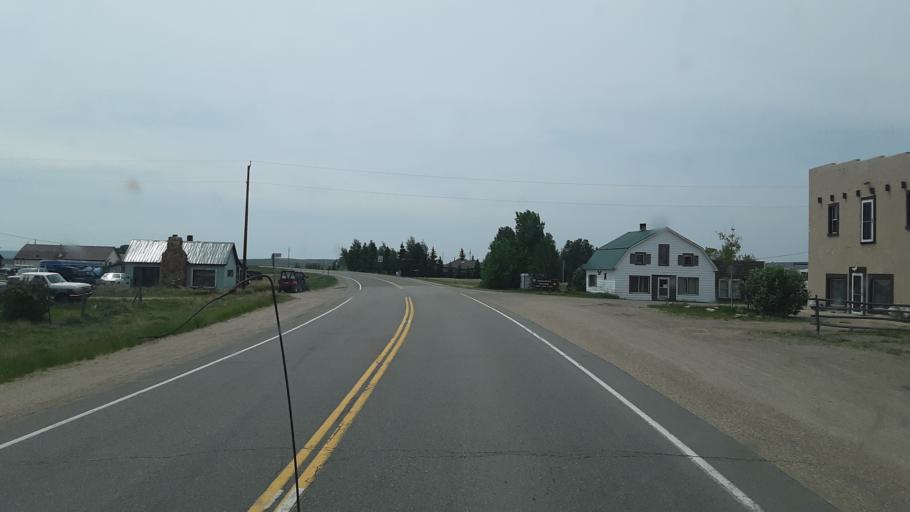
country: US
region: Colorado
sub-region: Jackson County
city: Walden
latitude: 40.8604
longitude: -106.3129
